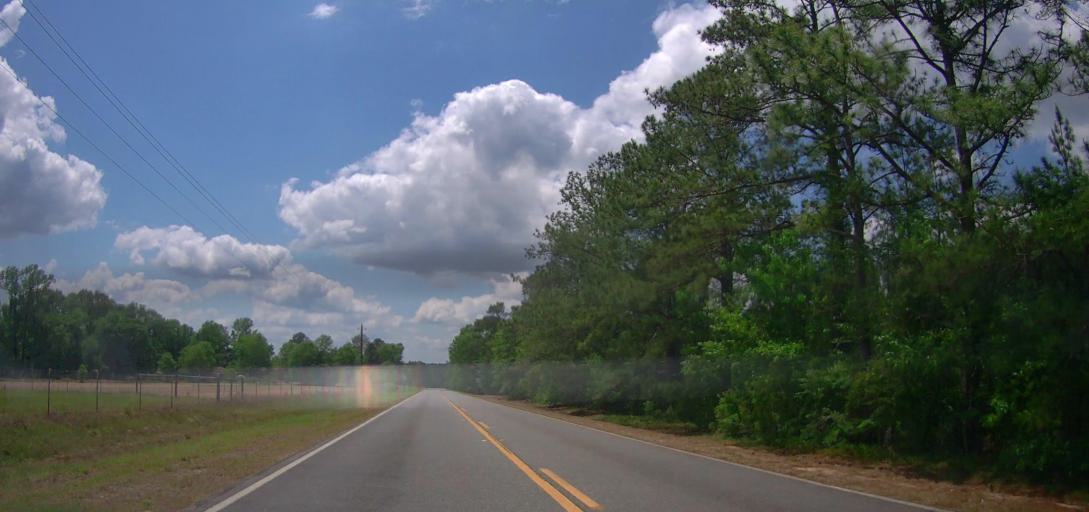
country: US
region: Georgia
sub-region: Laurens County
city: East Dublin
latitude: 32.5269
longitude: -82.7132
